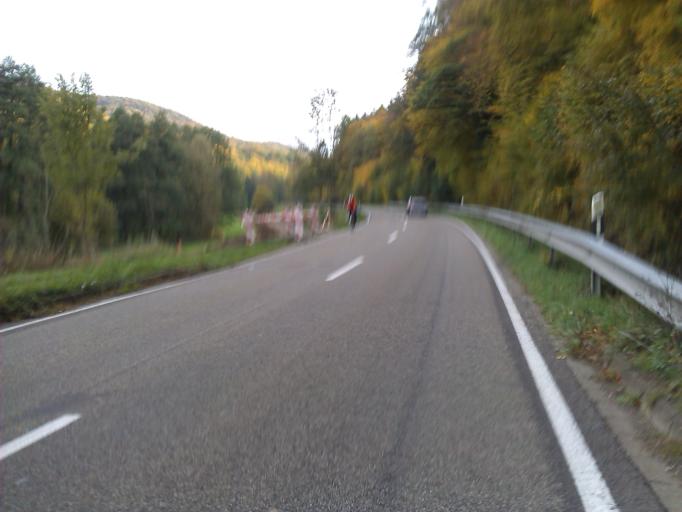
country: DE
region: Rheinland-Pfalz
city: Hefersweiler
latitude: 49.6003
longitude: 7.6877
